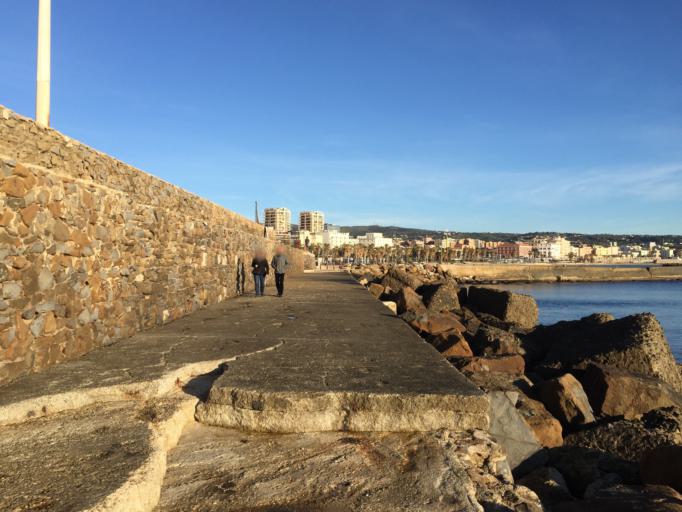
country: IT
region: Latium
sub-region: Citta metropolitana di Roma Capitale
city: Civitavecchia
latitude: 42.0890
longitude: 11.7896
